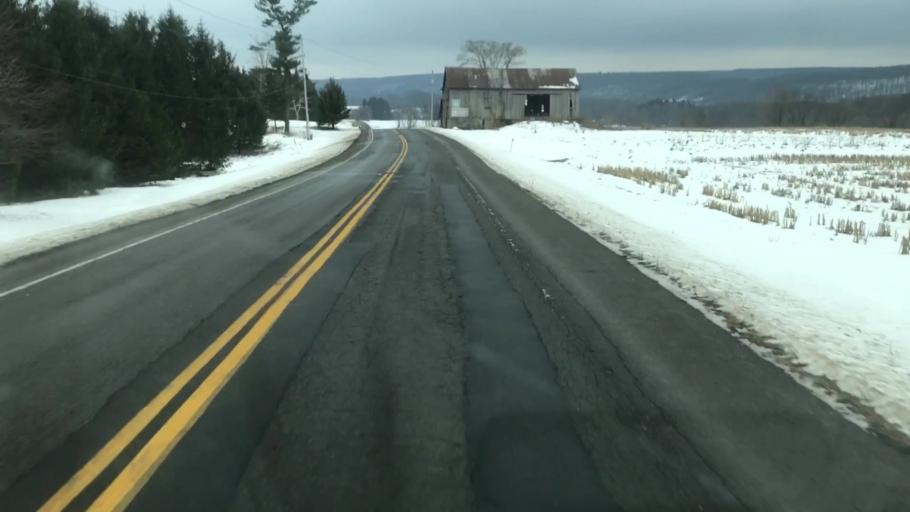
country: US
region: New York
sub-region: Cayuga County
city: Moravia
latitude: 42.7115
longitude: -76.3125
